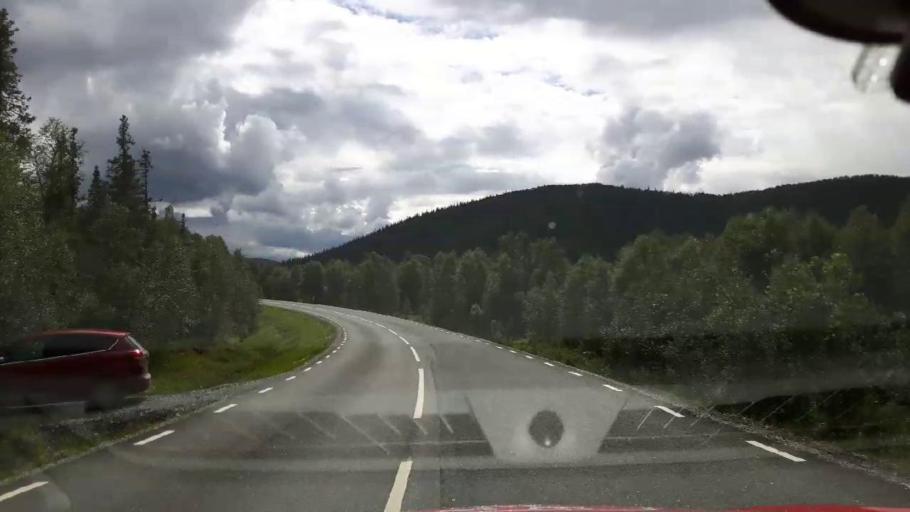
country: NO
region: Nord-Trondelag
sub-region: Royrvik
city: Royrvik
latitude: 64.8891
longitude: 14.1905
